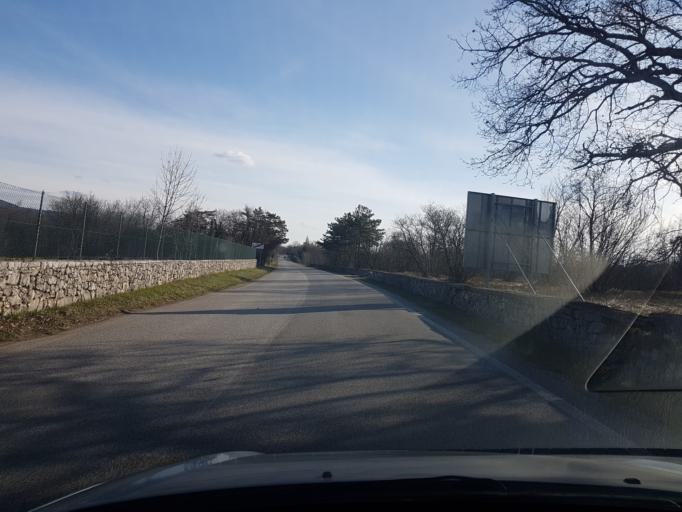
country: IT
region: Friuli Venezia Giulia
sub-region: Provincia di Trieste
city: Santa Croce
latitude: 45.7599
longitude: 13.7060
